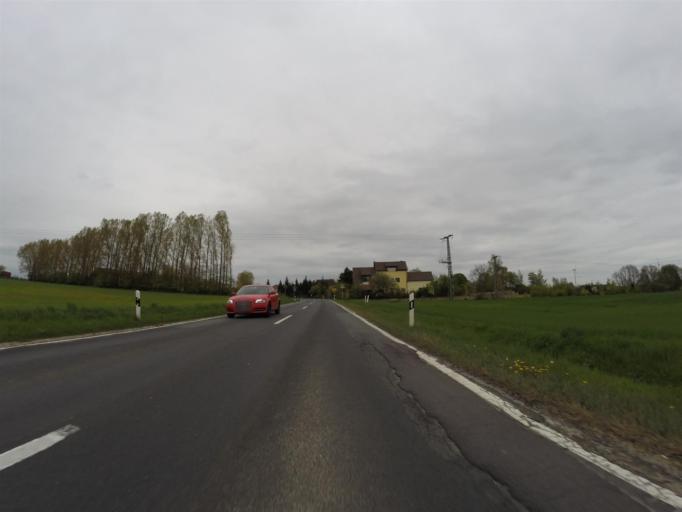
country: DE
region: Thuringia
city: Camburg
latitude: 51.0832
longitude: 11.7418
